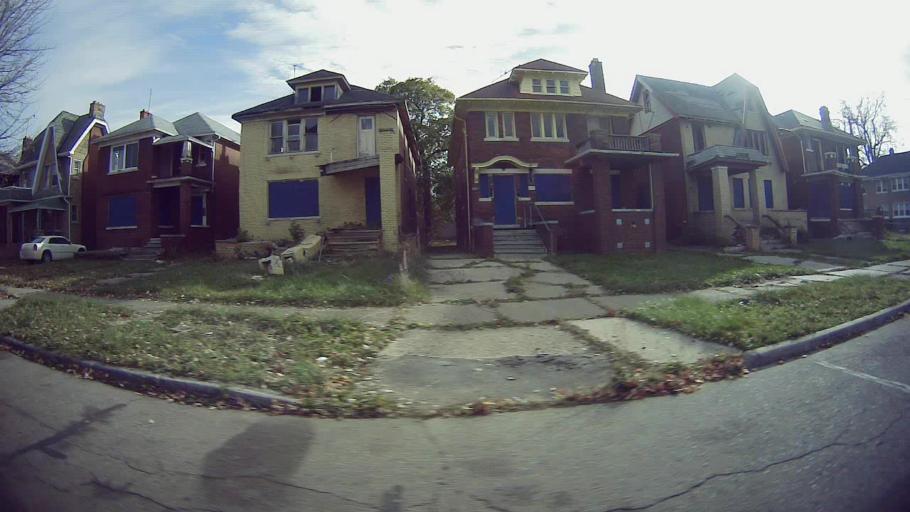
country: US
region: Michigan
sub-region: Wayne County
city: Highland Park
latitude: 42.3828
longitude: -83.1181
